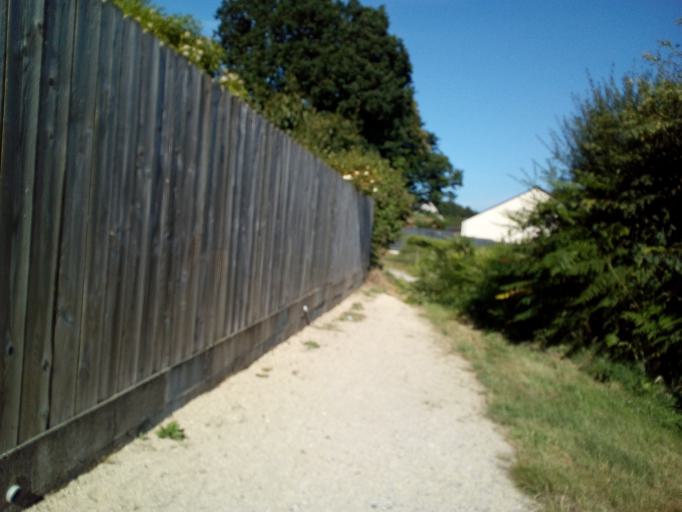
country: FR
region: Brittany
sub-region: Departement du Finistere
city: Landivisiau
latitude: 48.5070
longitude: -4.0872
